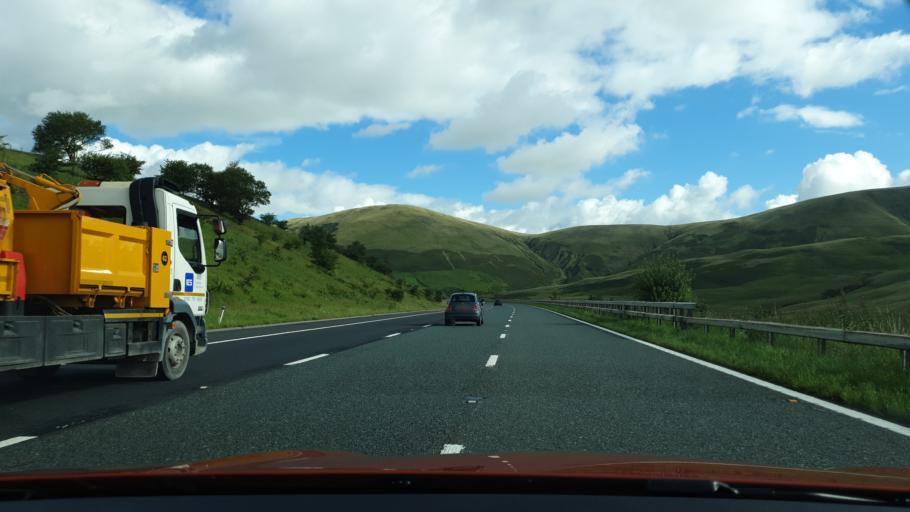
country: GB
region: England
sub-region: Cumbria
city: Sedbergh
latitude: 54.3779
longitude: -2.5828
